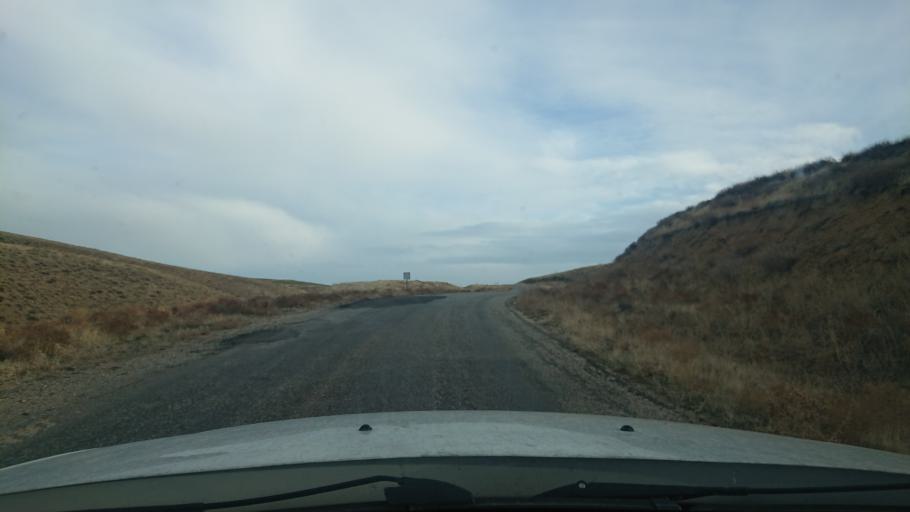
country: TR
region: Aksaray
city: Acipinar
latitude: 38.6321
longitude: 33.8005
